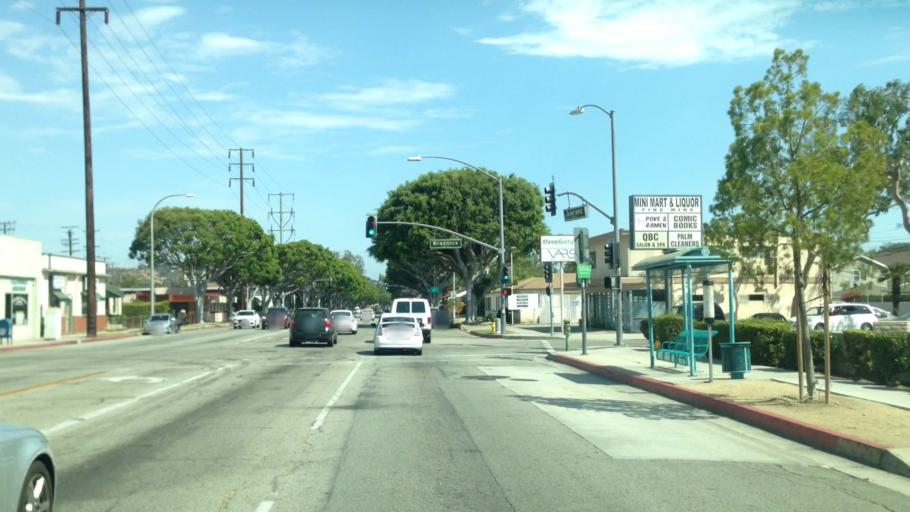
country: US
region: California
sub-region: Los Angeles County
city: Culver City
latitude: 34.0118
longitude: -118.4007
